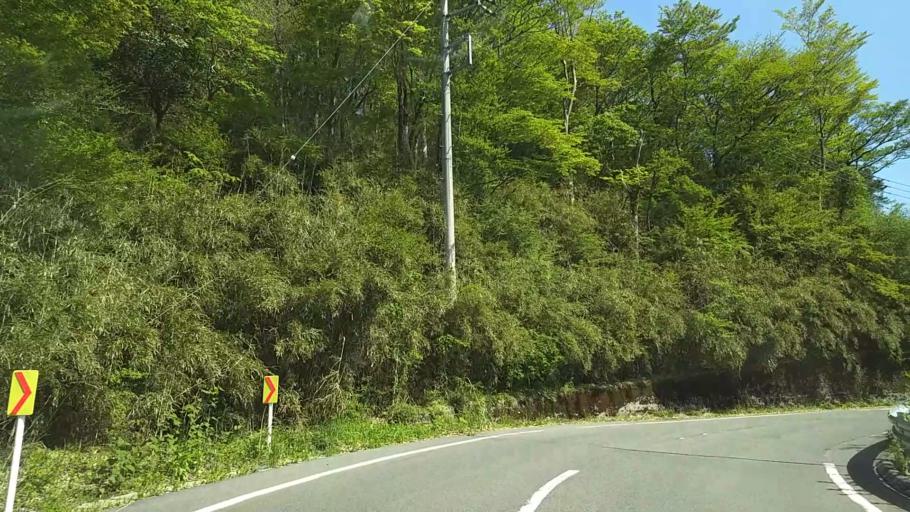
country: JP
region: Shizuoka
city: Gotemba
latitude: 35.2634
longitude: 138.9678
